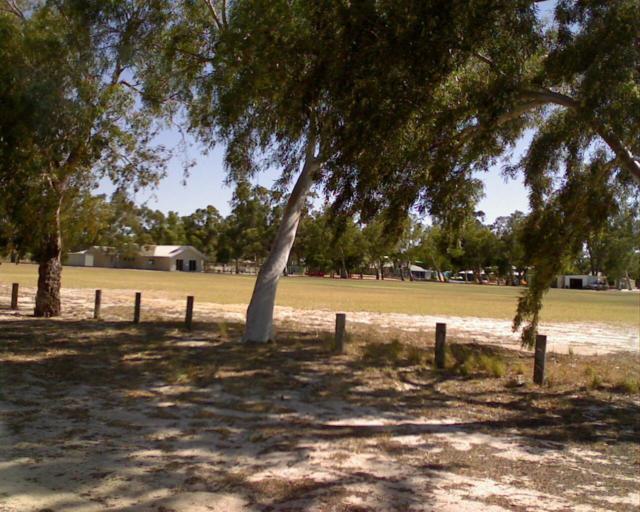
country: AU
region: Western Australia
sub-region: Dandaragan
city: Jurien Bay
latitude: -29.8206
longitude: 115.2671
